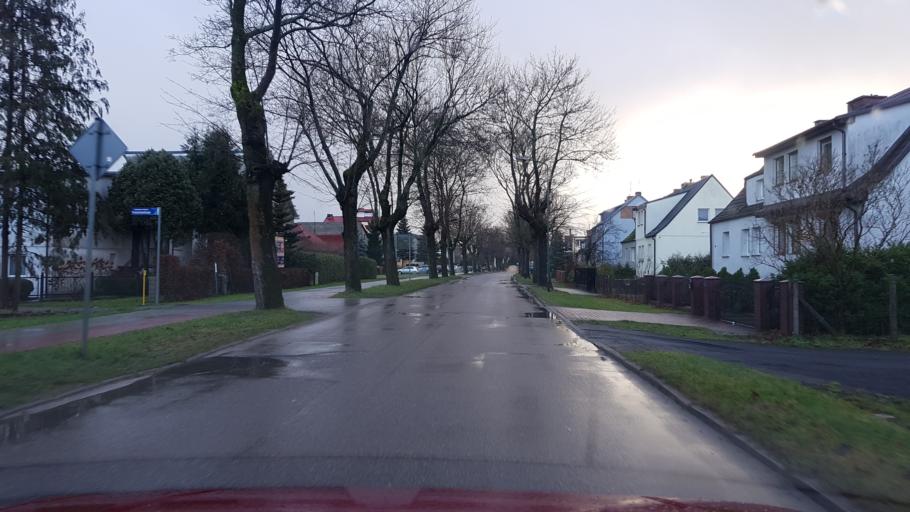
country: PL
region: West Pomeranian Voivodeship
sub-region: Powiat bialogardzki
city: Bialogard
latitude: 54.0183
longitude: 15.9884
